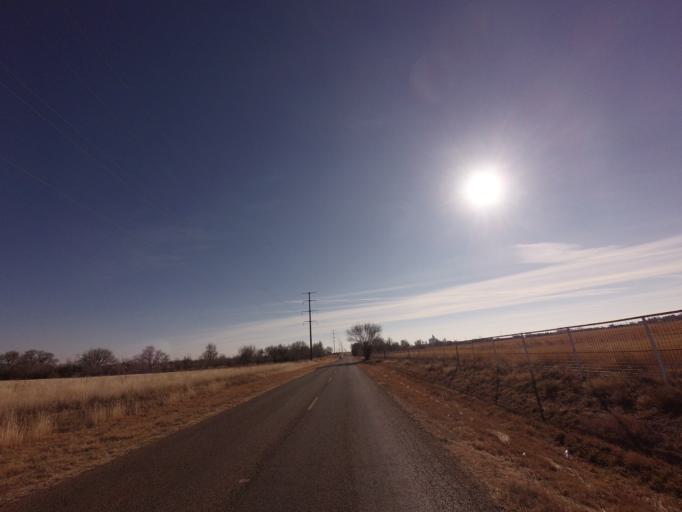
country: US
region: New Mexico
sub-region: Curry County
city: Clovis
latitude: 34.4183
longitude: -103.2493
